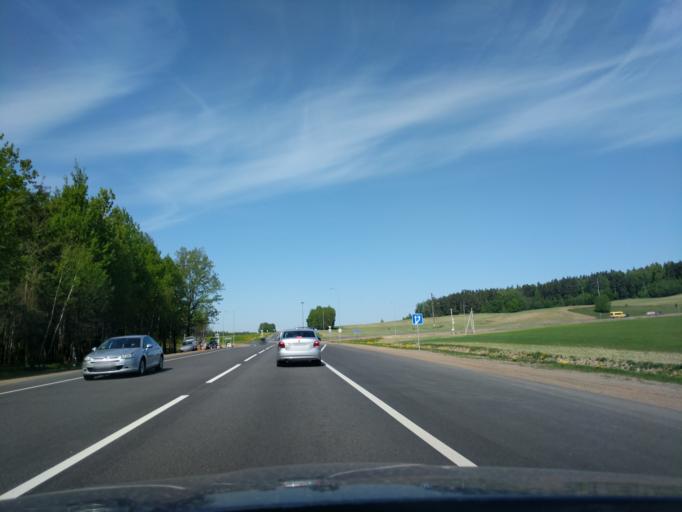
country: BY
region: Minsk
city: Bal'shavik
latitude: 54.0891
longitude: 27.5372
